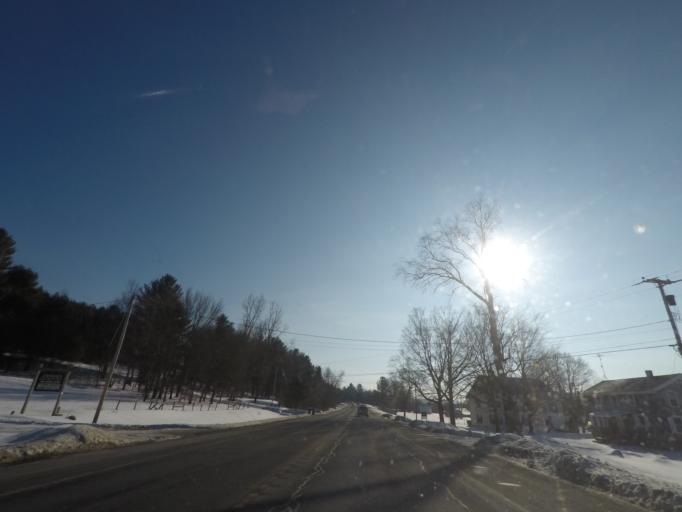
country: US
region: Massachusetts
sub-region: Berkshire County
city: Pittsfield
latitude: 42.5130
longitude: -73.3653
